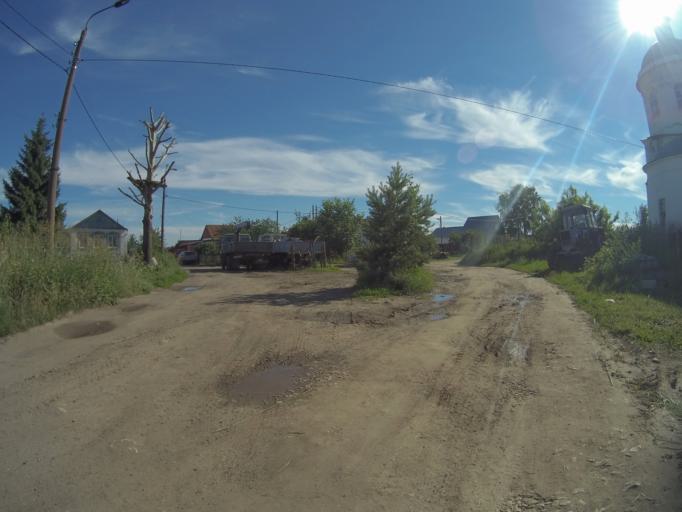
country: RU
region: Vladimir
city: Bogolyubovo
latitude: 56.2106
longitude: 40.5126
